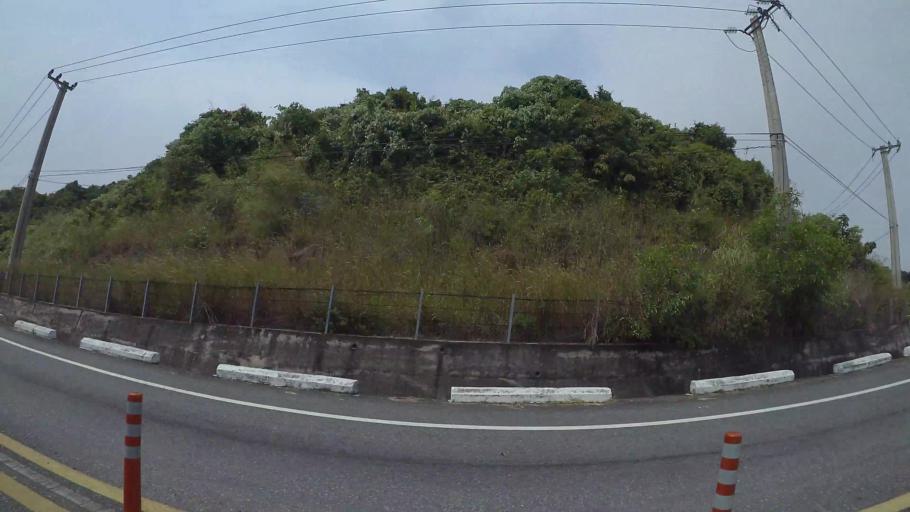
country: VN
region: Da Nang
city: Son Tra
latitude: 16.0984
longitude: 108.3064
